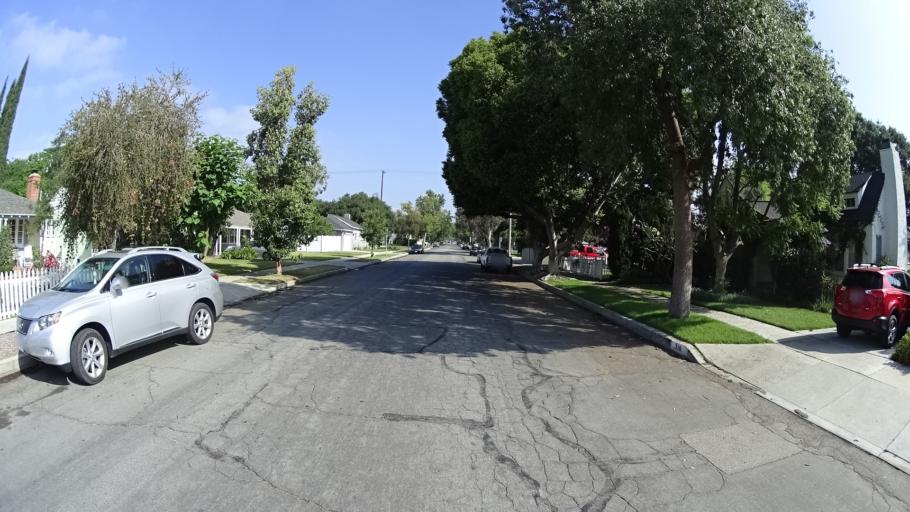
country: US
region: California
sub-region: Los Angeles County
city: Burbank
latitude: 34.1630
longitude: -118.3233
